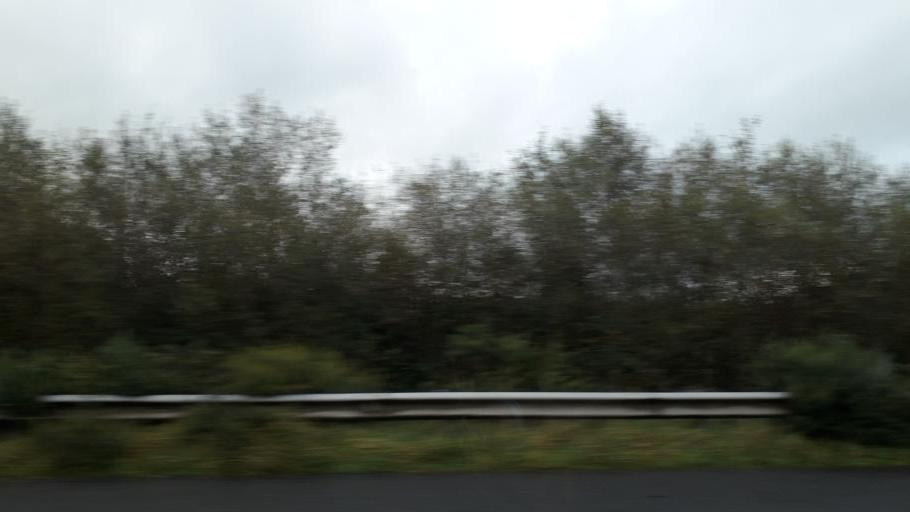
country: IE
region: Leinster
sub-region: An Longfort
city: Lanesborough
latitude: 53.7641
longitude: -8.0344
